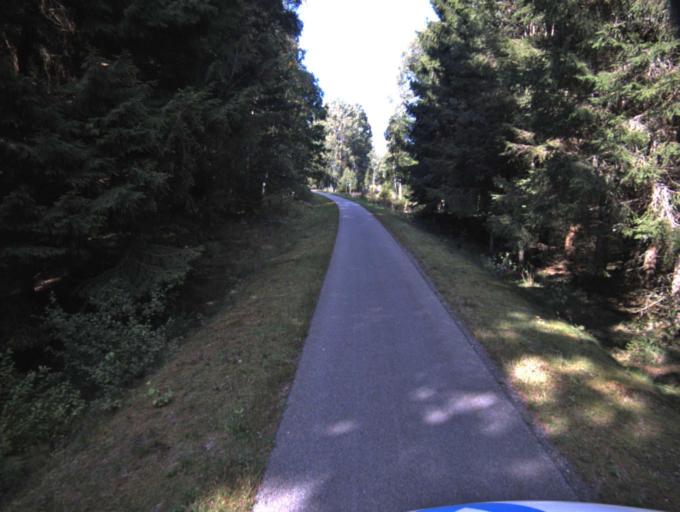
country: SE
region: Vaestra Goetaland
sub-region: Ulricehamns Kommun
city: Ulricehamn
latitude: 57.8295
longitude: 13.3448
